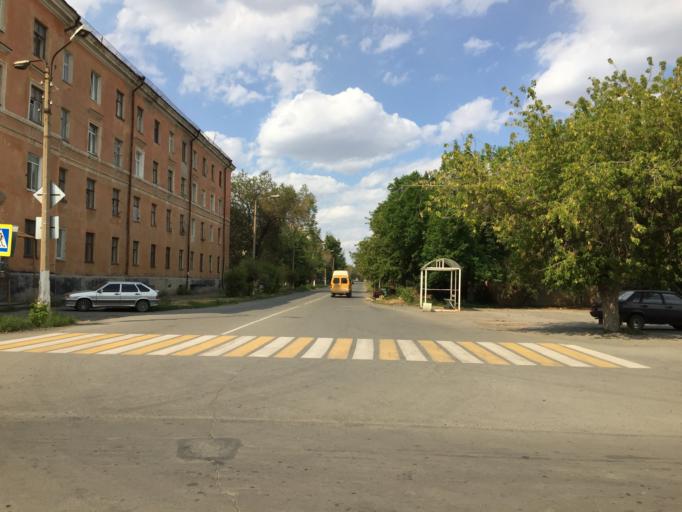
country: RU
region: Orenburg
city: Novotroitsk
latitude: 51.2033
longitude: 58.3038
